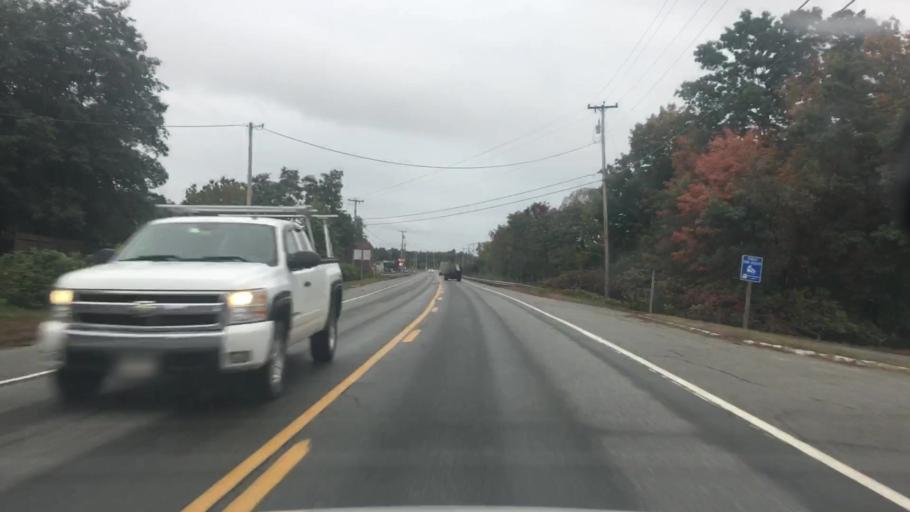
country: US
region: Maine
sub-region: Kennebec County
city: Belgrade
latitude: 44.4425
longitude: -69.8315
